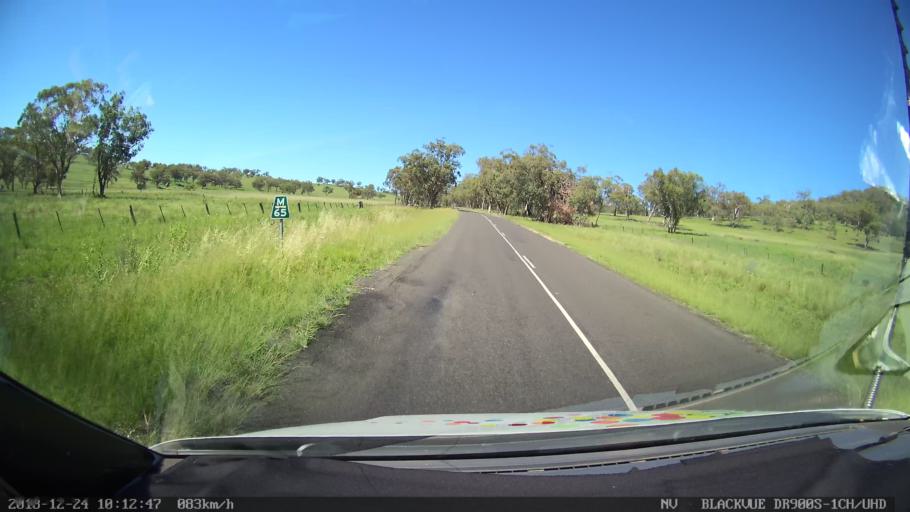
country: AU
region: New South Wales
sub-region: Liverpool Plains
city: Quirindi
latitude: -31.6827
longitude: 150.6447
